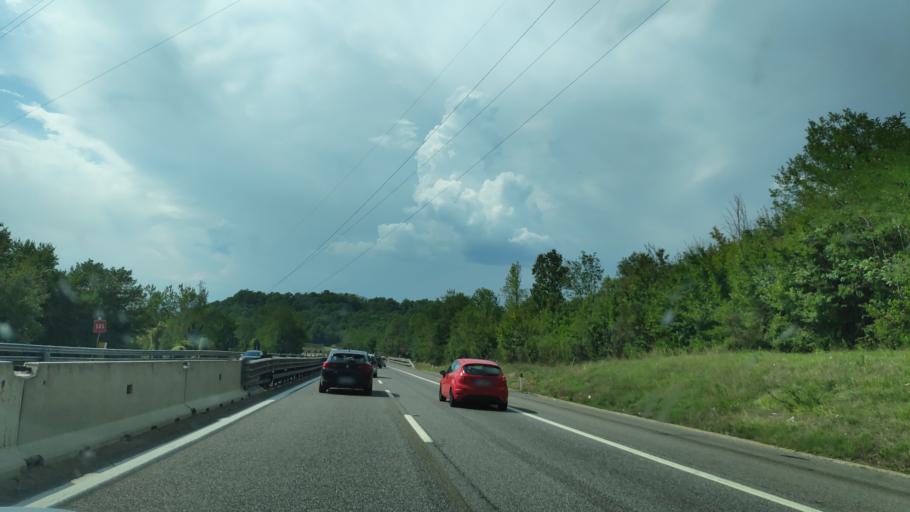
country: IT
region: Tuscany
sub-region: Province of Arezzo
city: Montalto
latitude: 43.5140
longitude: 11.6380
